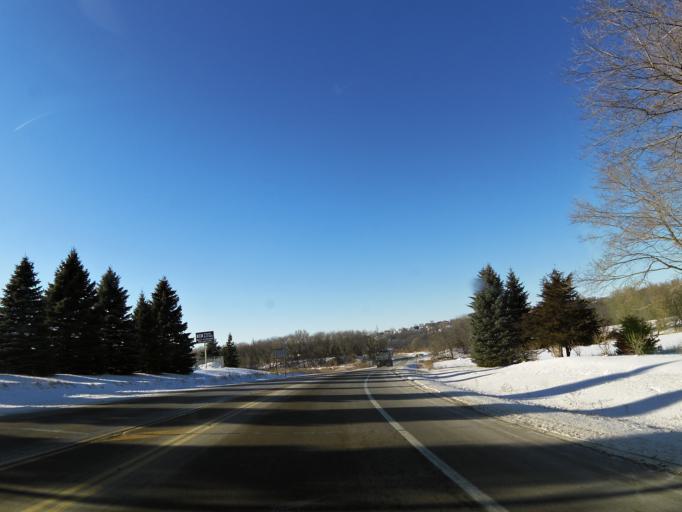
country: US
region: Minnesota
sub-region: Carver County
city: Chaska
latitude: 44.8059
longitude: -93.5667
